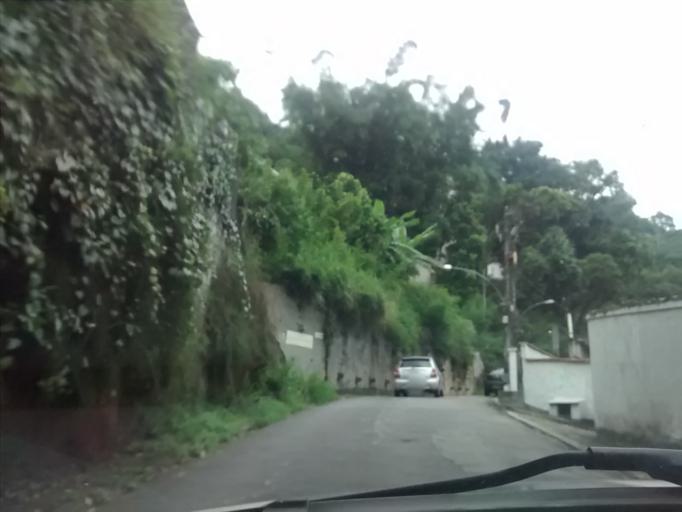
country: BR
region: Rio de Janeiro
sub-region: Rio De Janeiro
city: Rio de Janeiro
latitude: -22.9590
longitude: -43.2692
